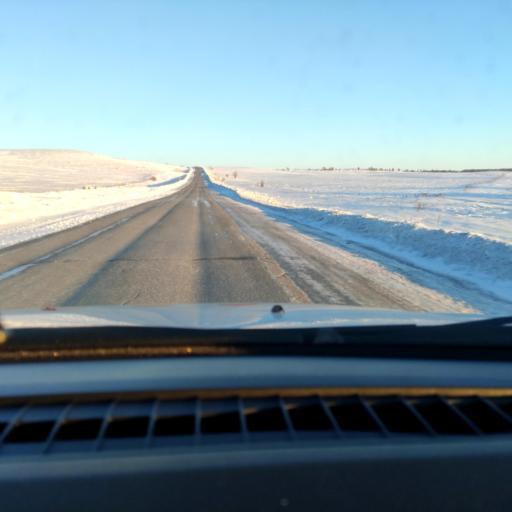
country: RU
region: Samara
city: Kinel'
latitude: 53.4405
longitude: 50.6576
